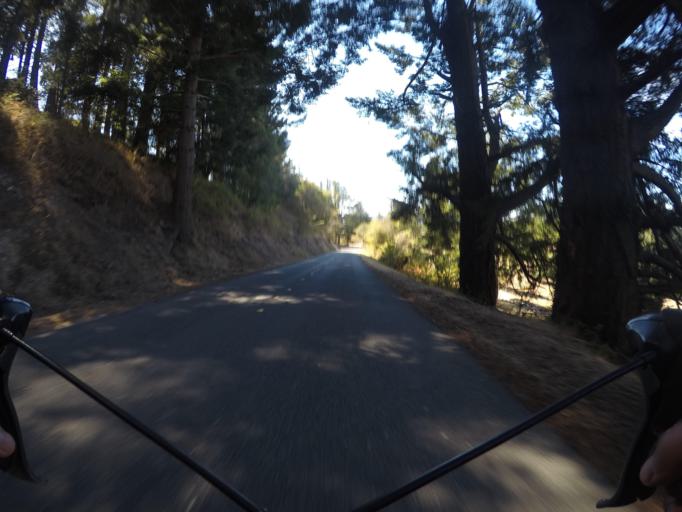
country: US
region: California
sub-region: San Mateo County
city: Portola Valley
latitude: 37.2878
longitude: -122.2165
